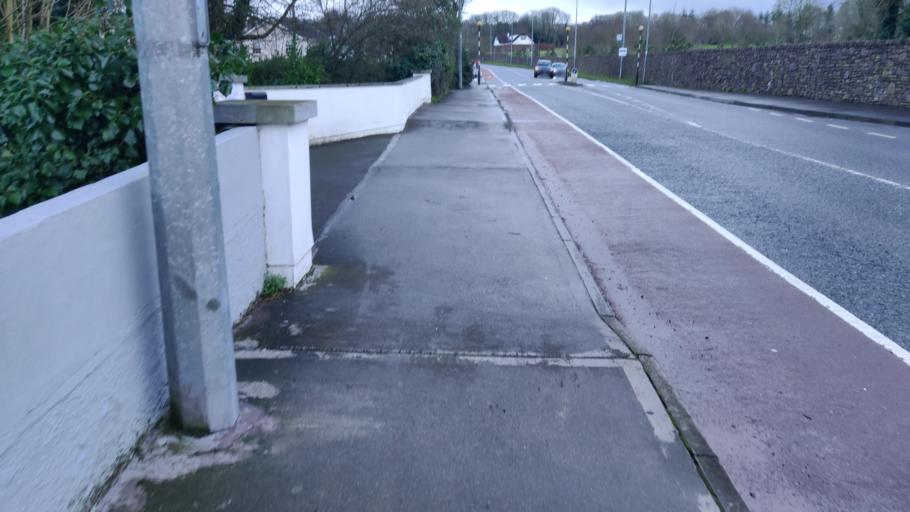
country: IE
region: Munster
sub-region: County Cork
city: Cork
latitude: 51.8698
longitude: -8.4176
